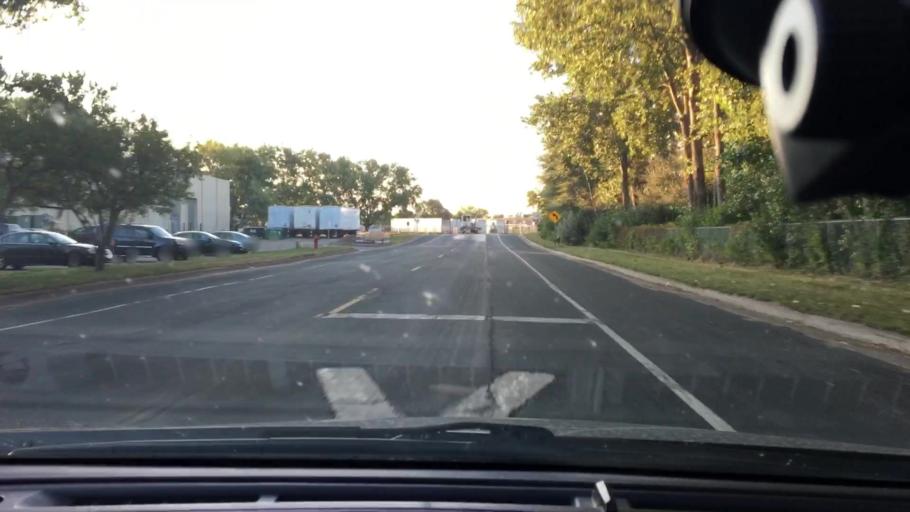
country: US
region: Minnesota
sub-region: Hennepin County
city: New Hope
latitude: 44.9898
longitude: -93.3980
